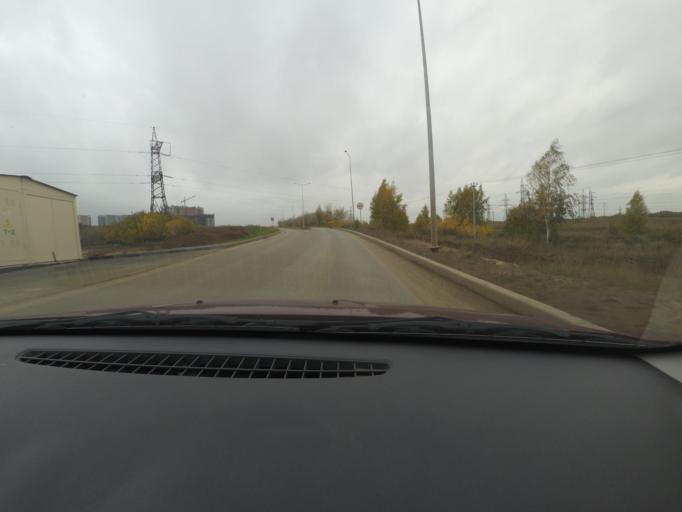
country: RU
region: Nizjnij Novgorod
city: Afonino
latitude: 56.2453
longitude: 44.0583
